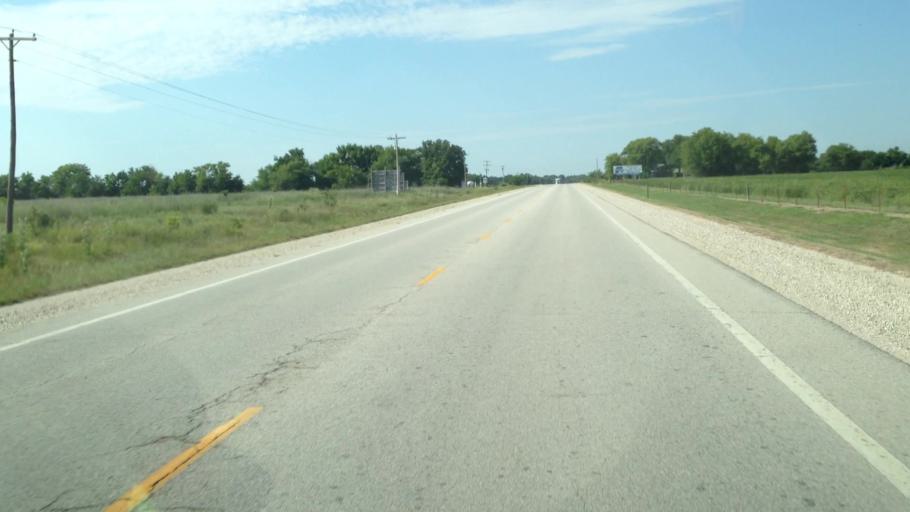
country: US
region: Kansas
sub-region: Neosho County
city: Erie
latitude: 37.5197
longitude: -95.2701
